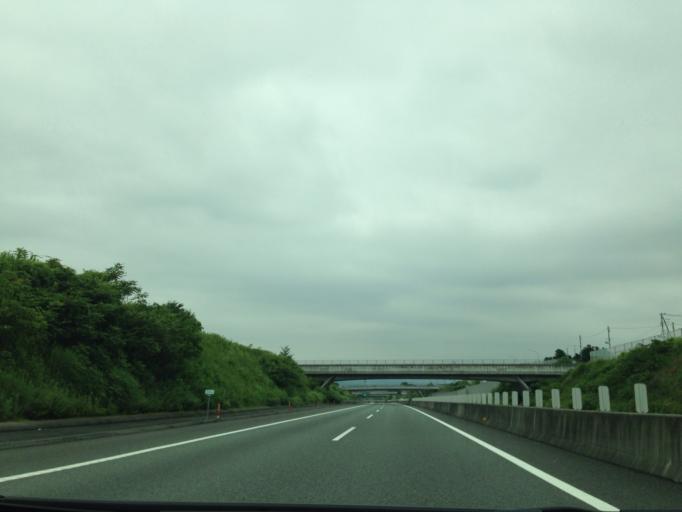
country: JP
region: Shizuoka
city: Fuji
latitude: 35.2000
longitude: 138.6879
